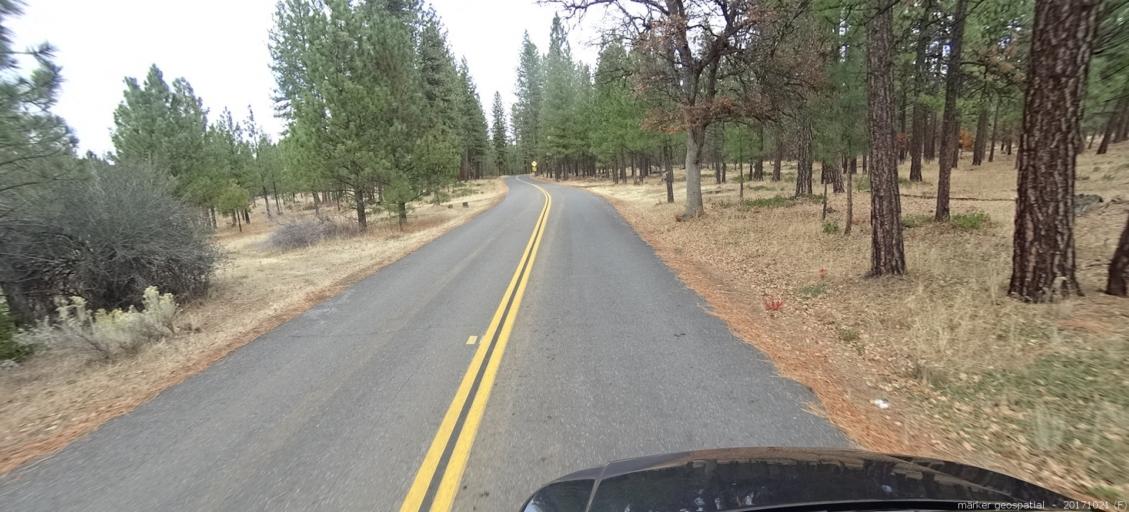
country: US
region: California
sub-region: Shasta County
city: Burney
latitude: 40.9329
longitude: -121.6428
